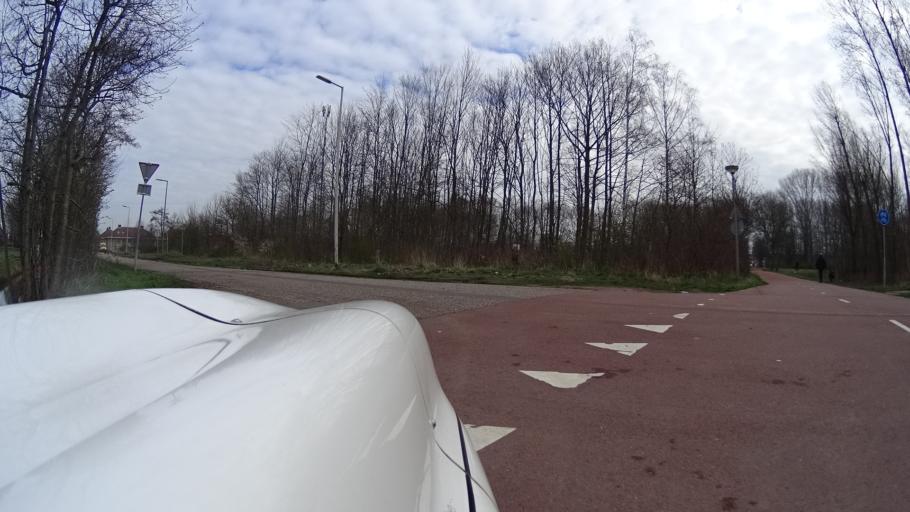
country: NL
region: South Holland
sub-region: Gemeente Capelle aan den IJssel
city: Capelle-West
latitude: 51.8985
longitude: 4.5577
